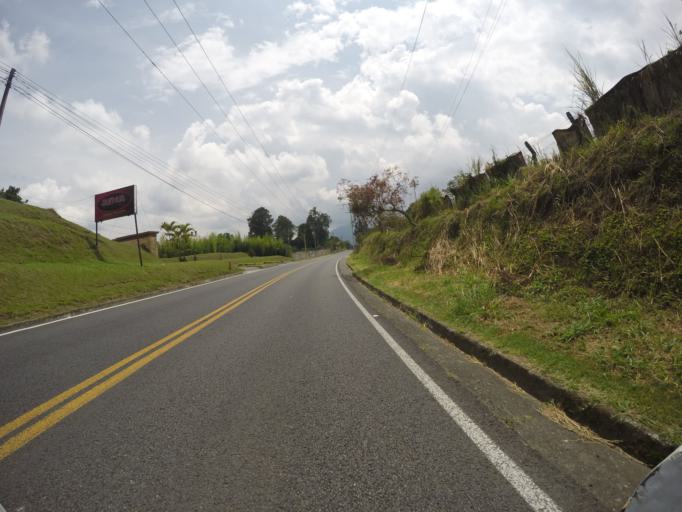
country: CO
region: Risaralda
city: Pereira
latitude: 4.7713
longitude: -75.6914
